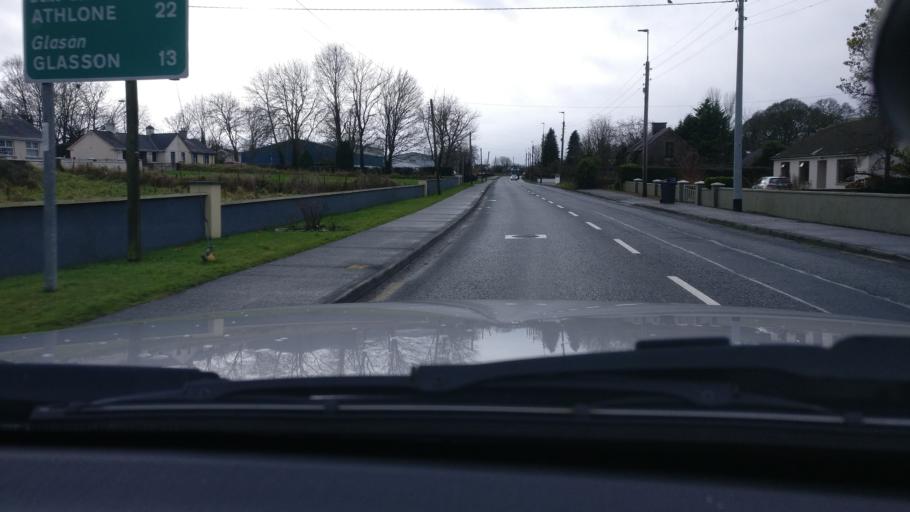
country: IE
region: Leinster
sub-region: An Longfort
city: Ballymahon
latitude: 53.5604
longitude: -7.7633
